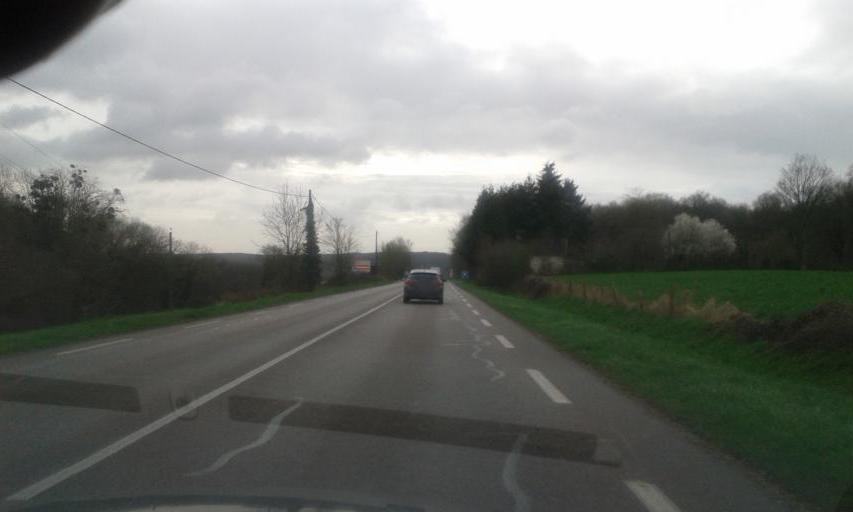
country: FR
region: Haute-Normandie
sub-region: Departement de l'Eure
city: Fleury-sur-Andelle
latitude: 49.3727
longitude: 1.3340
